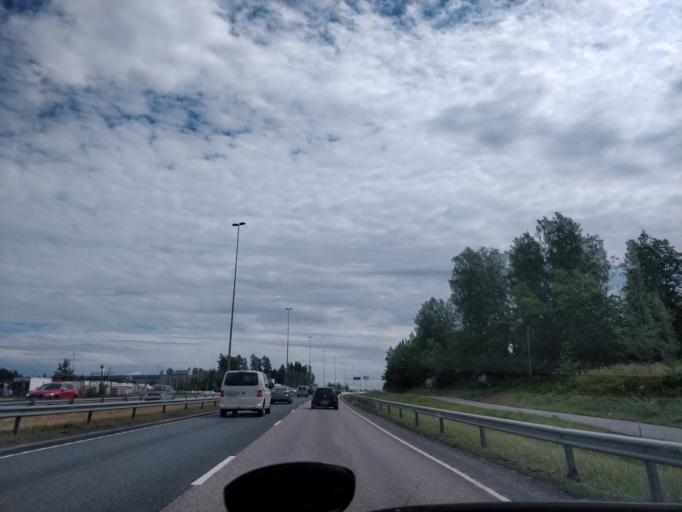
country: FI
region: Uusimaa
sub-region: Helsinki
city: Teekkarikylae
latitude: 60.2982
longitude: 24.9022
